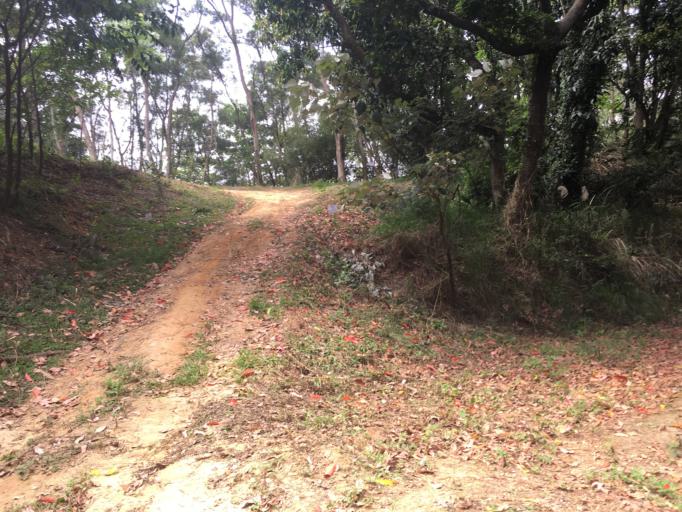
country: TW
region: Taiwan
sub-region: Hsinchu
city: Hsinchu
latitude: 24.7438
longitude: 120.9783
